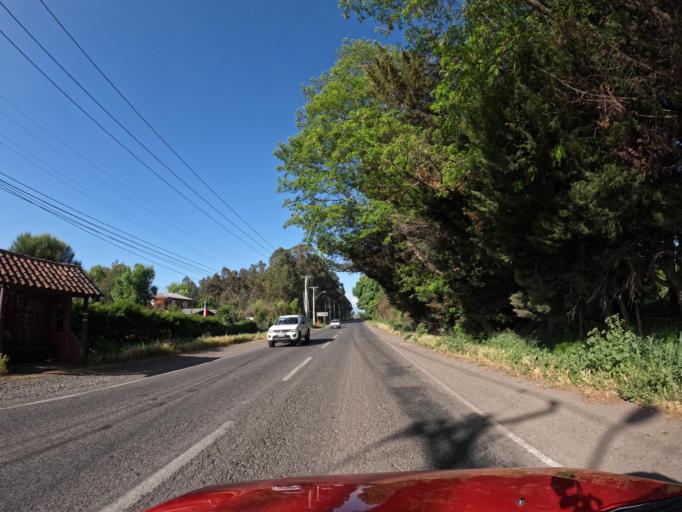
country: CL
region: Maule
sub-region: Provincia de Curico
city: Teno
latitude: -34.8670
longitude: -71.2100
